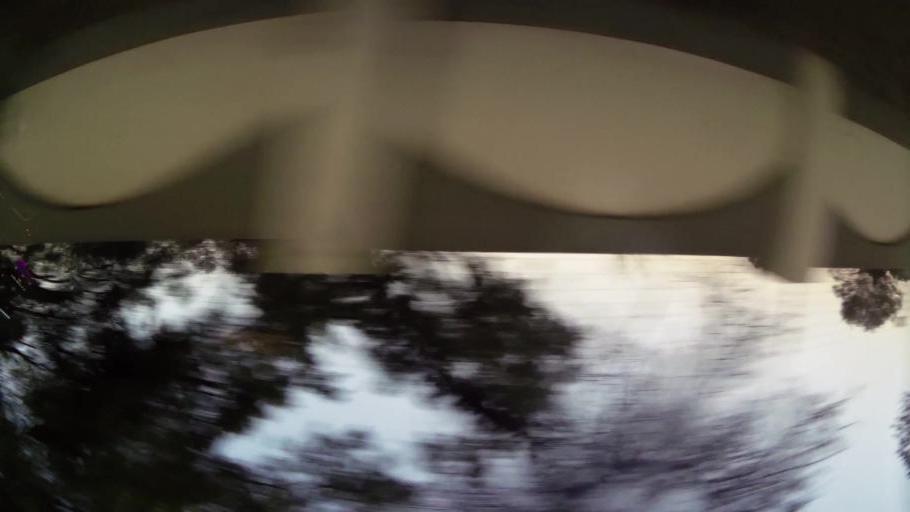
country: ZA
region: Gauteng
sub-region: City of Tshwane Metropolitan Municipality
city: Centurion
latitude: -25.8462
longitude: 28.1194
